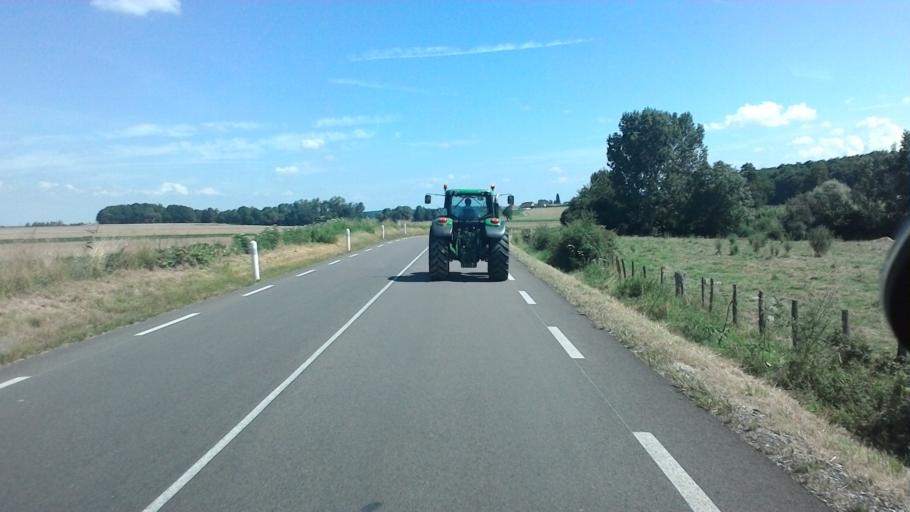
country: FR
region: Bourgogne
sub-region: Departement de la Cote-d'Or
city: Seurre
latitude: 46.9242
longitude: 5.1224
